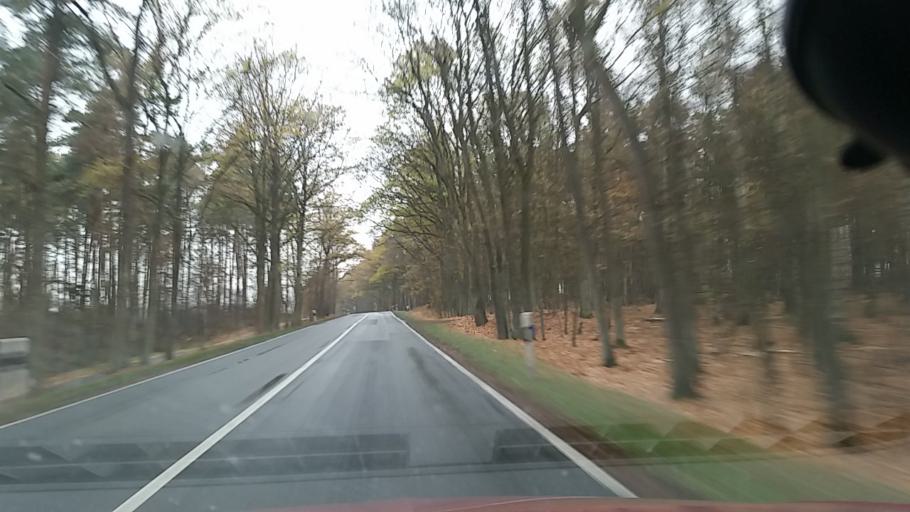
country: DE
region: Lower Saxony
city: Wieren
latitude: 52.8678
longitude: 10.6741
